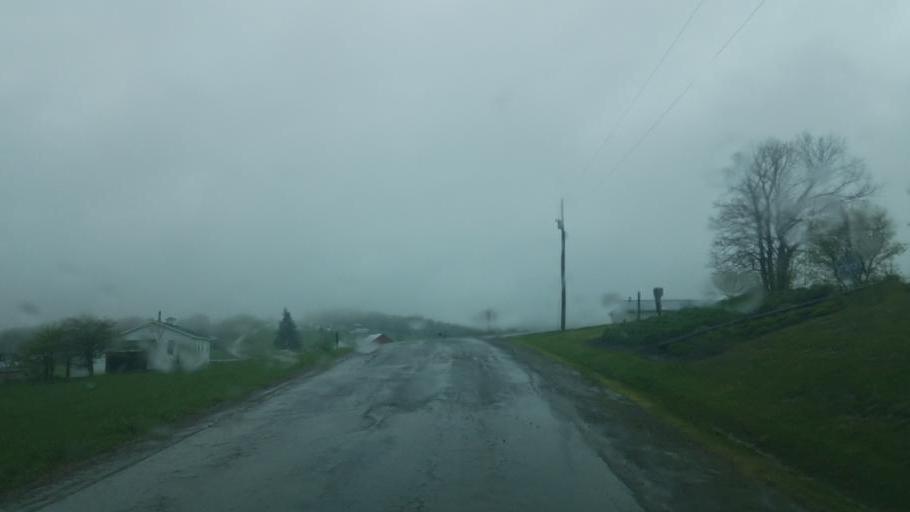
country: US
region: New York
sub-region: Steuben County
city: Canisteo
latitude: 42.1083
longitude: -77.5259
